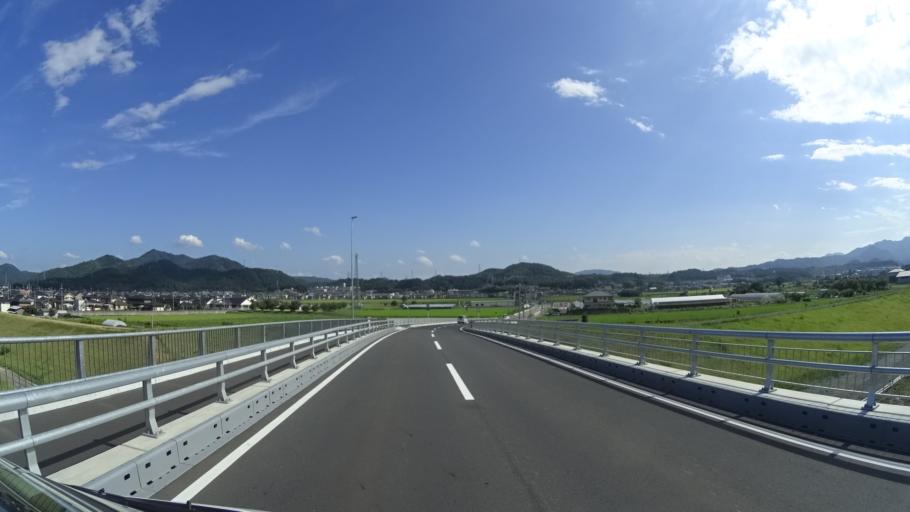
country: JP
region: Kyoto
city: Fukuchiyama
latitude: 35.3086
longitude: 135.1707
